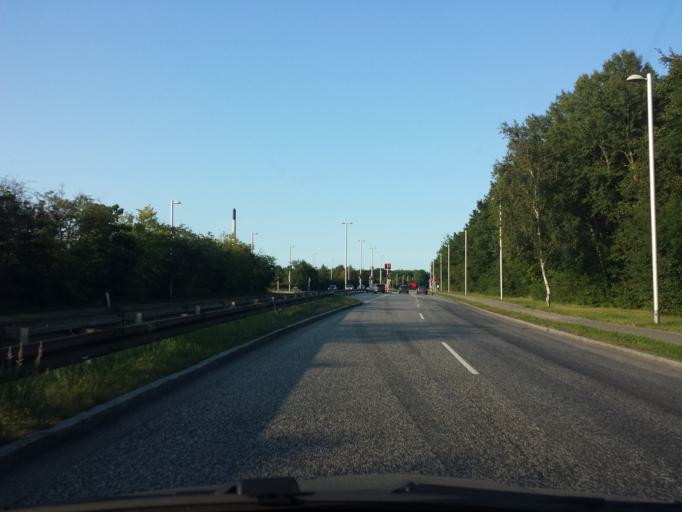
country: DK
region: Capital Region
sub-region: Glostrup Kommune
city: Glostrup
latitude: 55.6965
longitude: 12.4127
